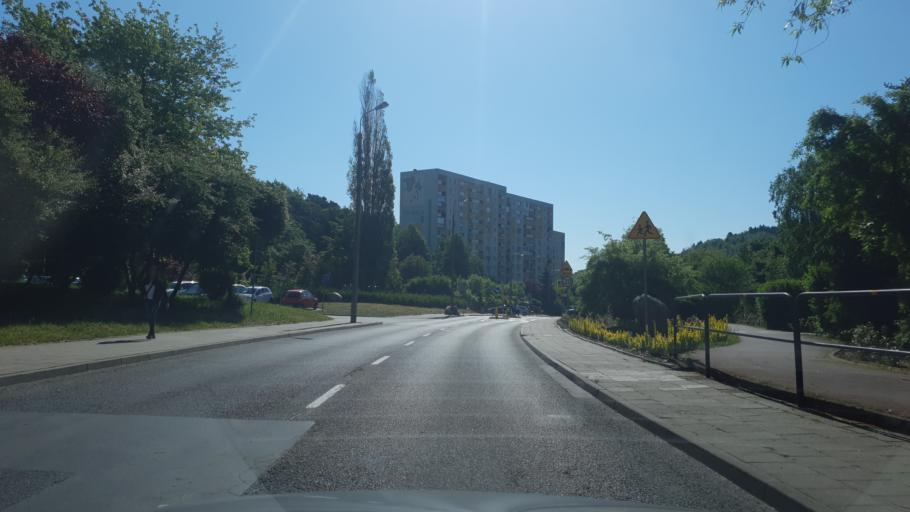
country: PL
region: Pomeranian Voivodeship
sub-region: Sopot
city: Sopot
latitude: 54.4576
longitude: 18.5359
